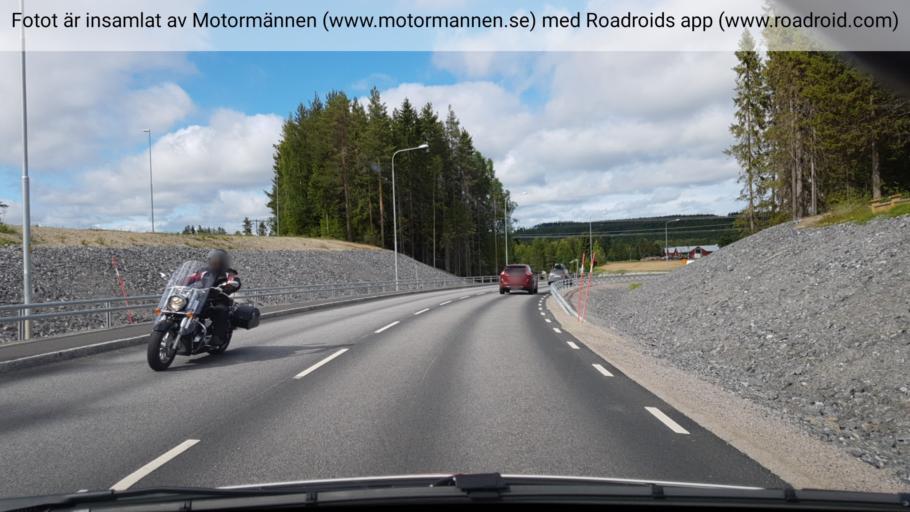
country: SE
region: Vaesterbotten
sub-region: Vannas Kommun
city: Vaennaes
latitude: 63.9120
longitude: 19.7695
